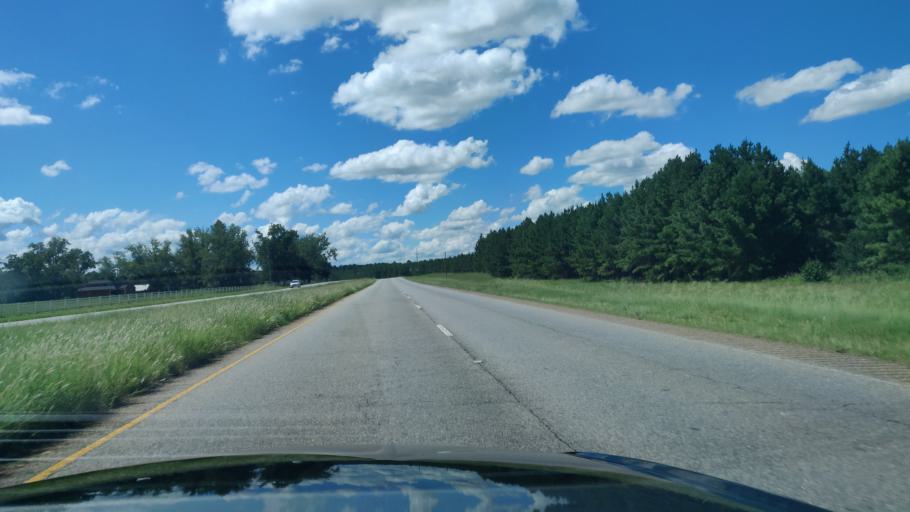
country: US
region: Georgia
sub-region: Stewart County
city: Richland
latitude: 32.0188
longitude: -84.6628
